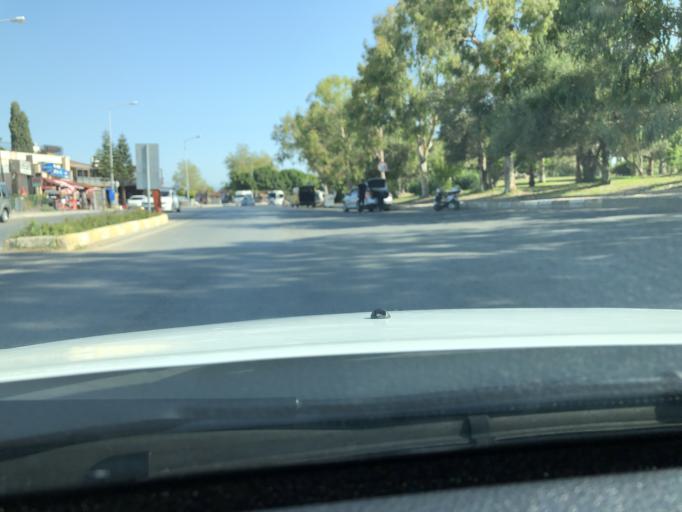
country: TR
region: Antalya
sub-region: Manavgat
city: Side
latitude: 36.7725
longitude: 31.3946
